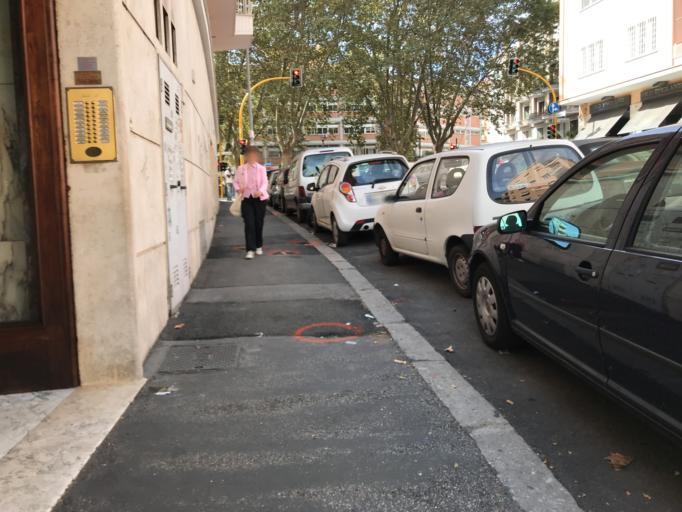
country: VA
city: Vatican City
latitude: 41.9135
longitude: 12.4422
